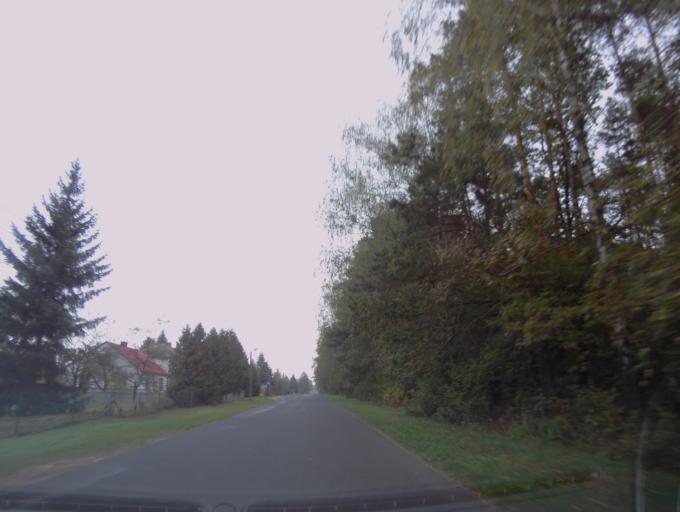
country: PL
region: Subcarpathian Voivodeship
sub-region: Powiat nizanski
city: Harasiuki
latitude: 50.4556
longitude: 22.4123
